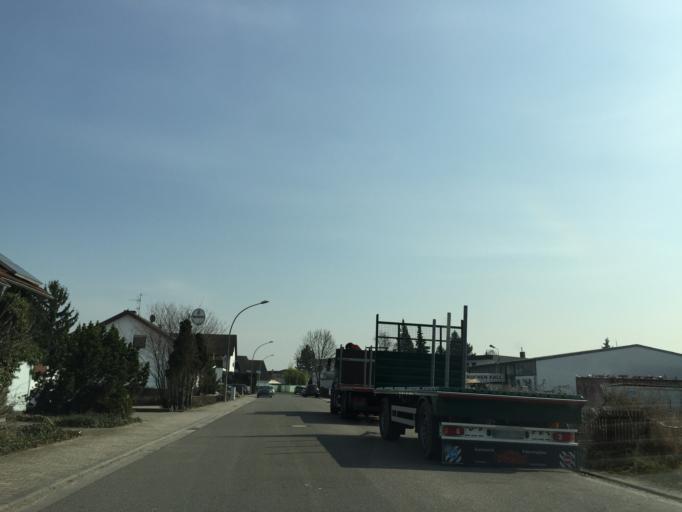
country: DE
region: Baden-Wuerttemberg
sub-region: Karlsruhe Region
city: Schwetzingen
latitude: 49.3761
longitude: 8.5825
